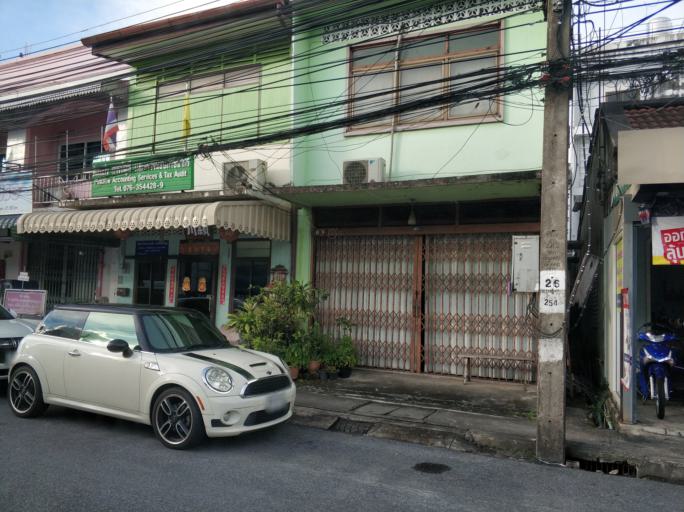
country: TH
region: Phuket
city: Wichit
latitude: 7.8867
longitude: 98.3745
